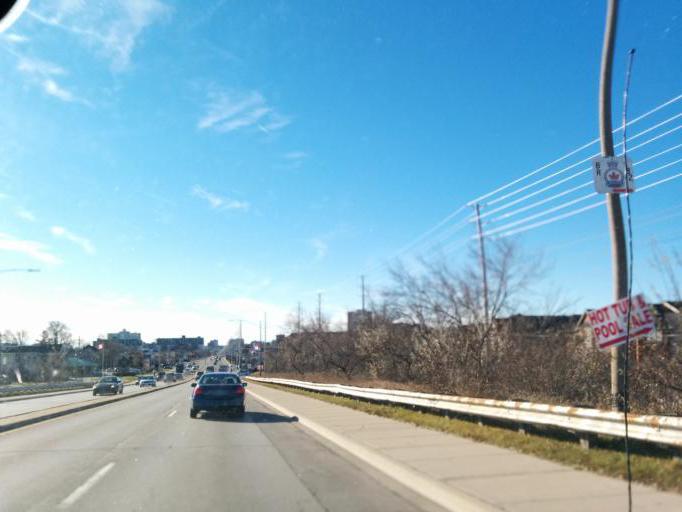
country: CA
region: Ontario
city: Mississauga
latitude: 43.5905
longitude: -79.6048
